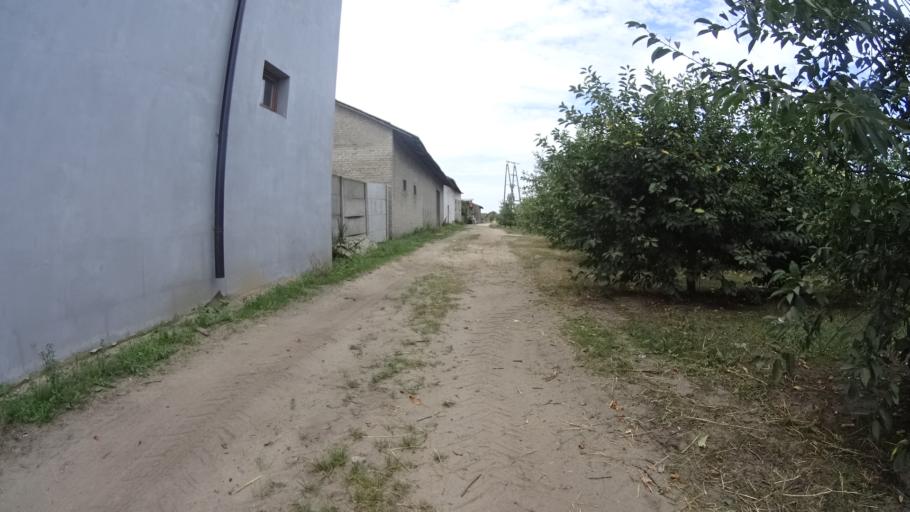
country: PL
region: Masovian Voivodeship
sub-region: Powiat bialobrzeski
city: Wysmierzyce
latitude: 51.6519
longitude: 20.7994
